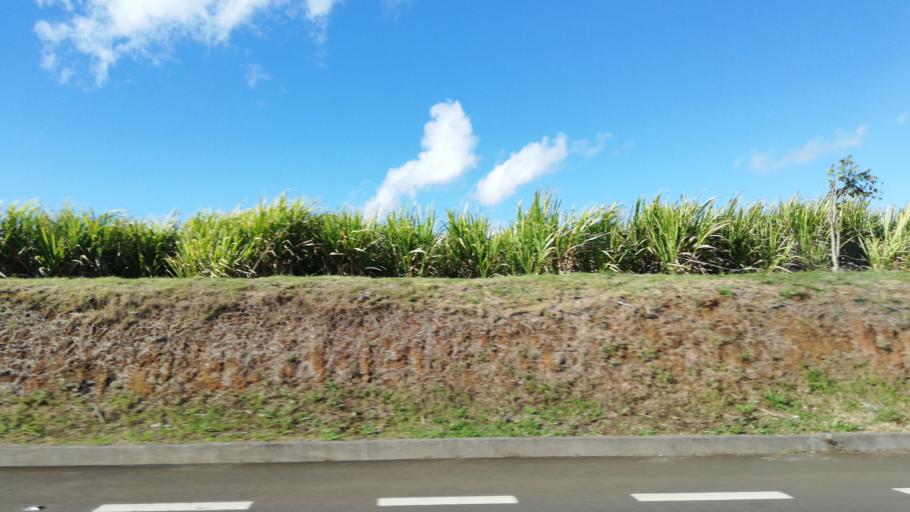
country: MU
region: Moka
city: Saint Pierre
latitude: -20.2318
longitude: 57.5226
